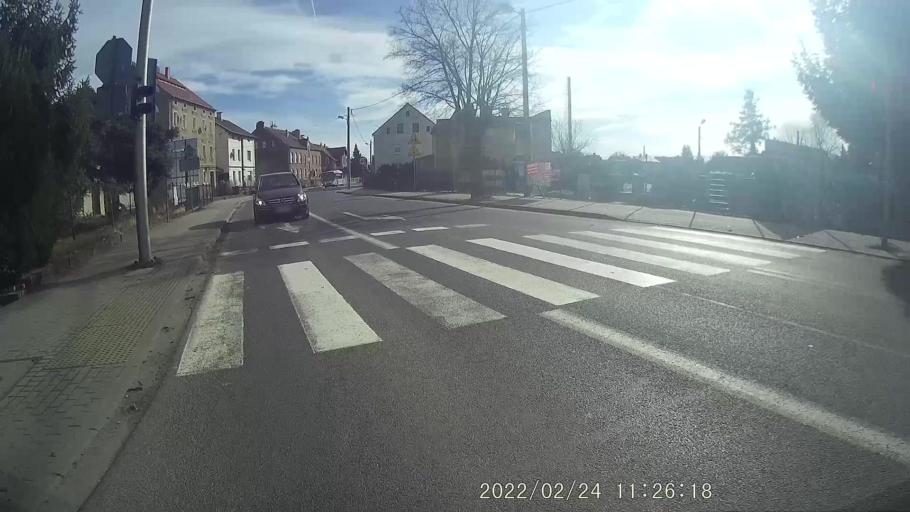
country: PL
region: Lubusz
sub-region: Powiat zaganski
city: Szprotawa
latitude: 51.5347
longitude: 15.6321
